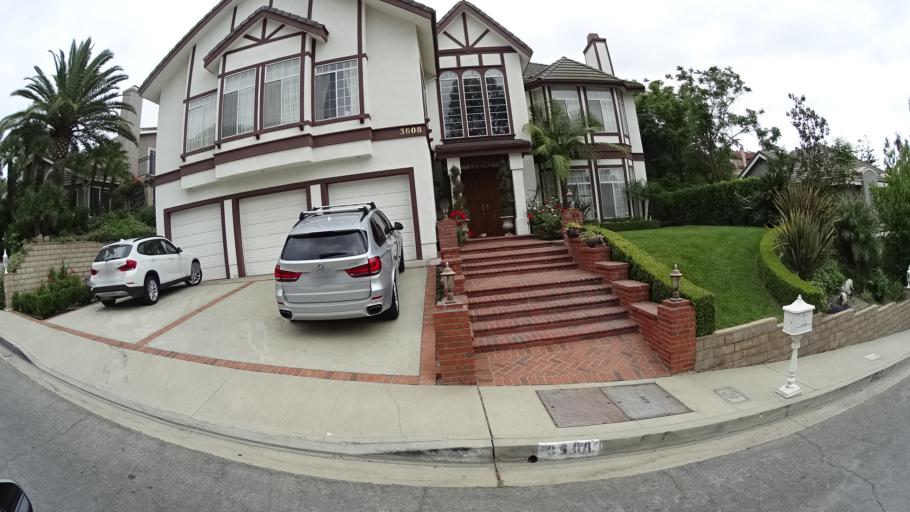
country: US
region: California
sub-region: Los Angeles County
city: Burbank
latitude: 34.2110
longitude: -118.3192
